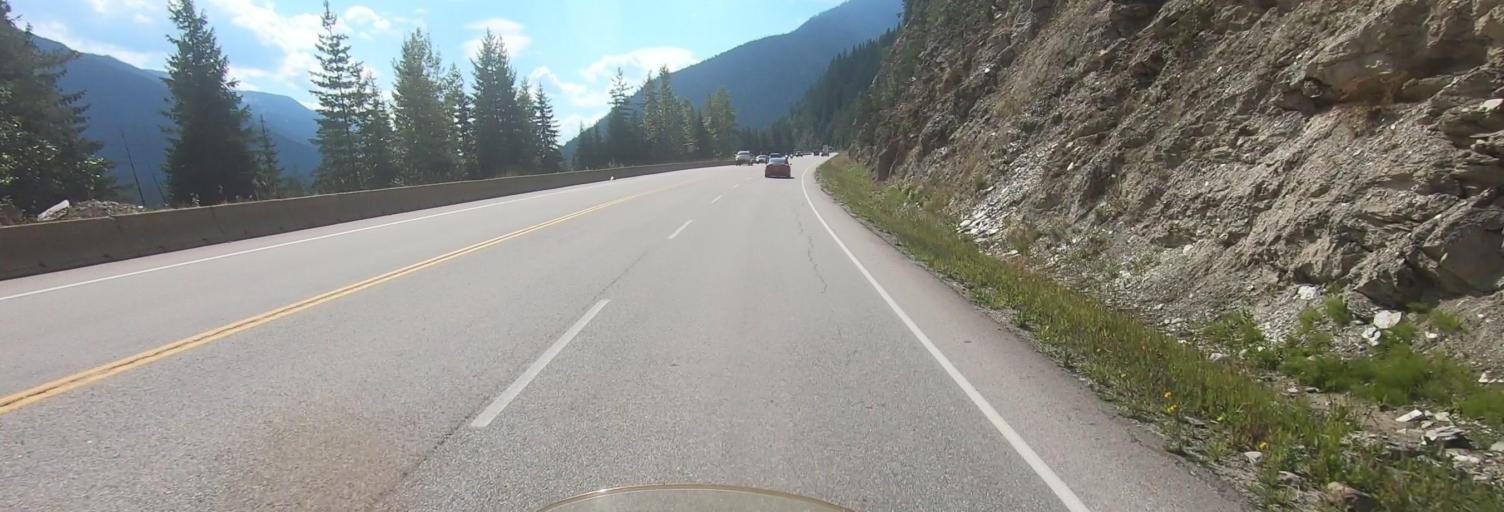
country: CA
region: British Columbia
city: Golden
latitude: 51.3604
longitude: -117.4387
